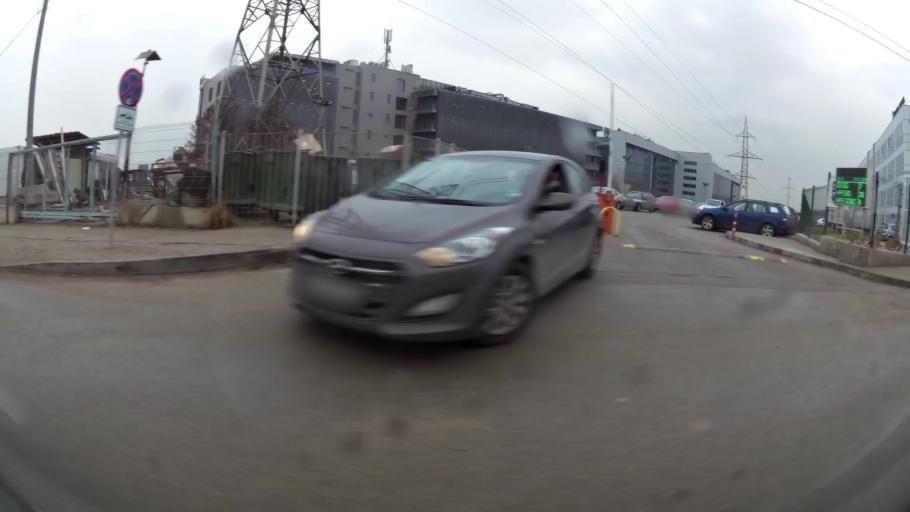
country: BG
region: Sofia-Capital
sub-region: Stolichna Obshtina
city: Sofia
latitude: 42.6219
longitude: 23.3775
